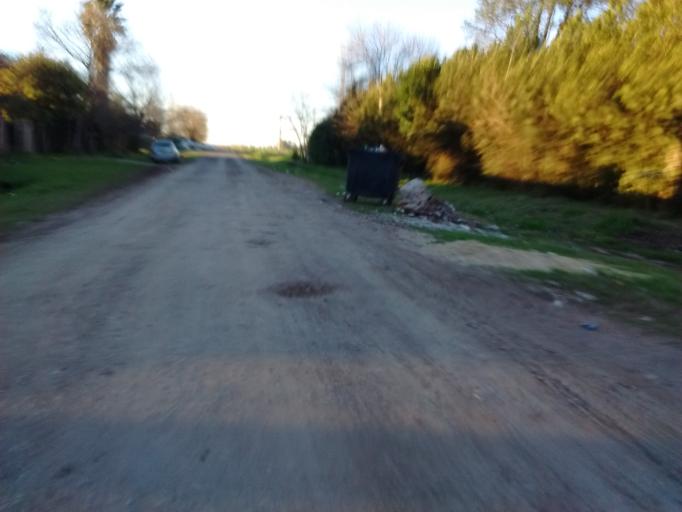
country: AR
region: Santa Fe
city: Funes
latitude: -32.9137
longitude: -60.8518
